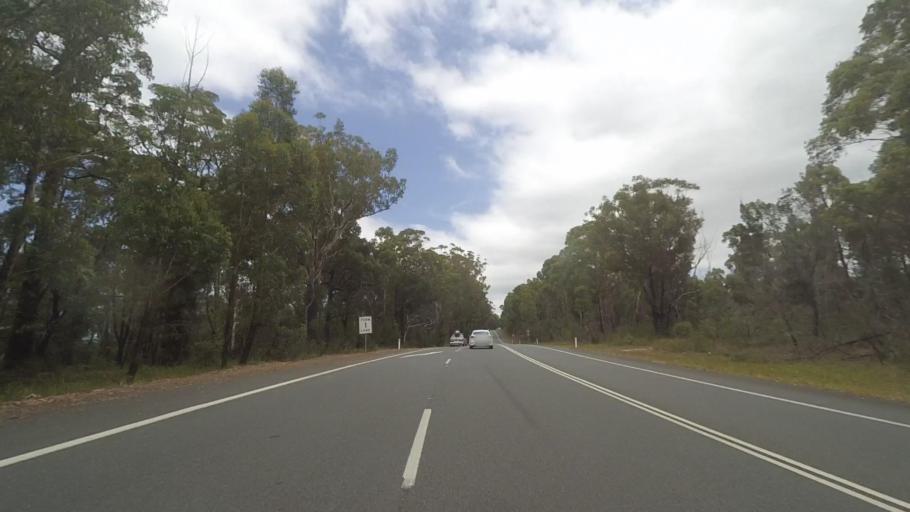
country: AU
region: New South Wales
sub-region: Shoalhaven Shire
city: Milton
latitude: -35.1414
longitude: 150.4643
